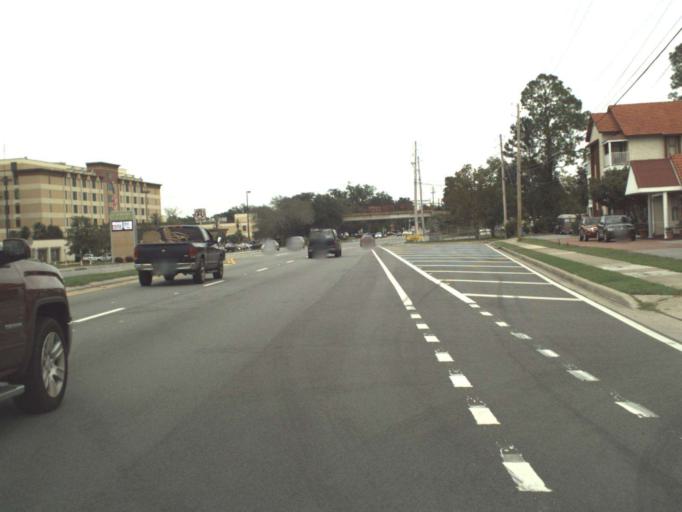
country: US
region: Florida
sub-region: Escambia County
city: Ferry Pass
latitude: 30.5128
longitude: -87.2186
